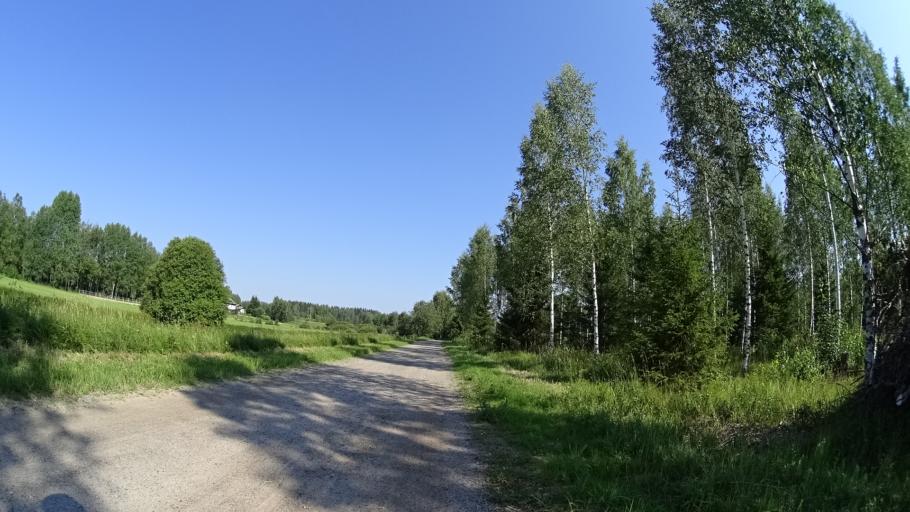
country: FI
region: Uusimaa
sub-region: Helsinki
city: Kerava
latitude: 60.3578
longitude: 25.1249
